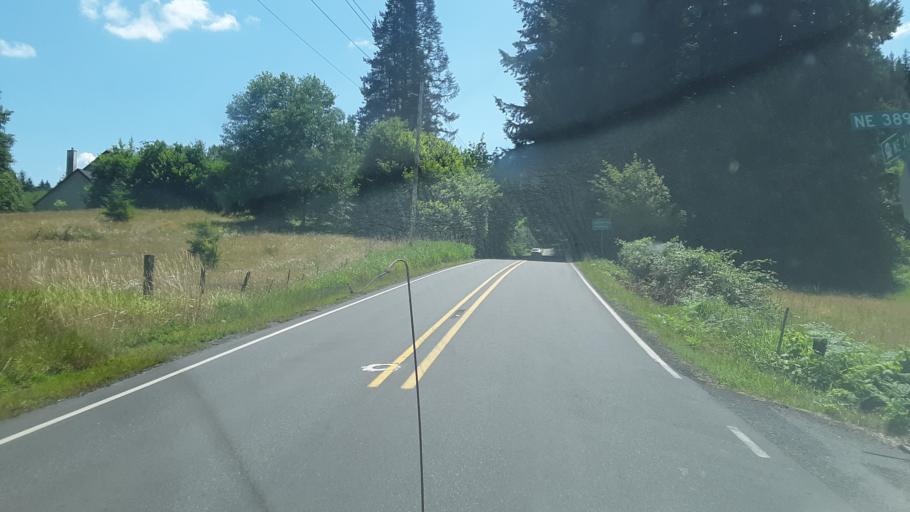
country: US
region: Washington
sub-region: Clark County
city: Amboy
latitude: 45.9030
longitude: -122.4520
